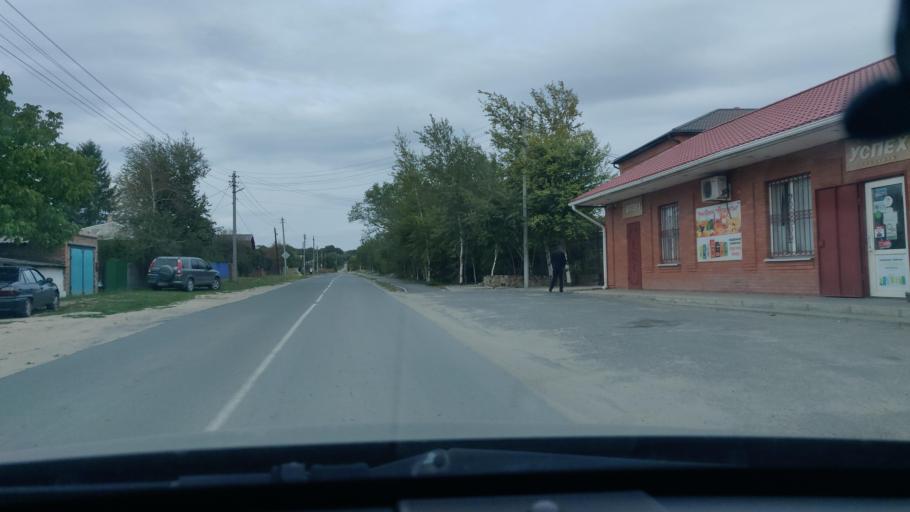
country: RU
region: Rostov
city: Ust'-Donetskiy
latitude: 47.6605
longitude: 40.9193
